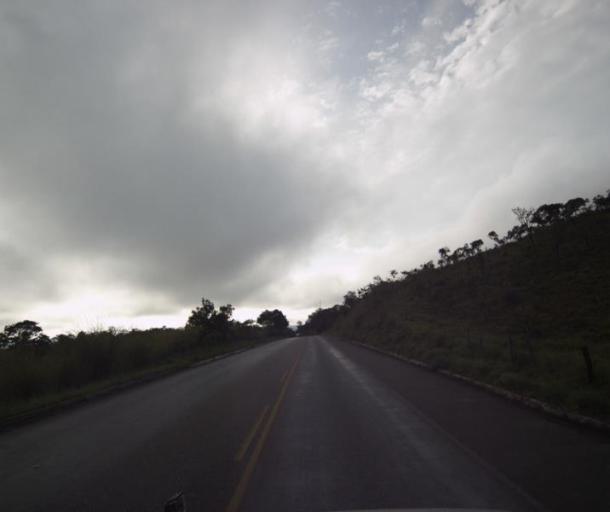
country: BR
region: Goias
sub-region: Pirenopolis
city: Pirenopolis
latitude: -15.7536
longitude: -48.7354
